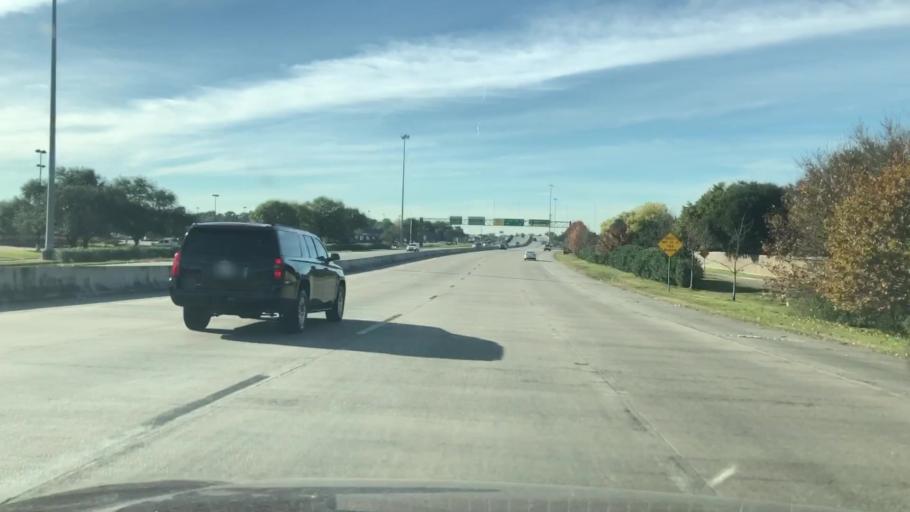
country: US
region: Texas
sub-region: Harris County
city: Bellaire
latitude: 29.6755
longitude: -95.4600
